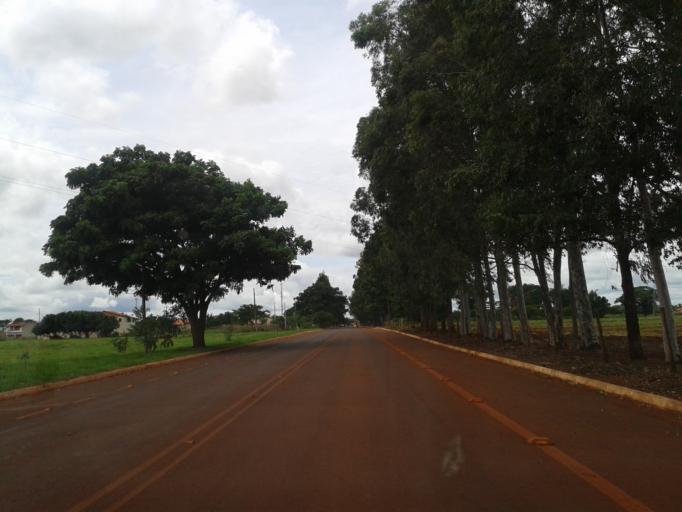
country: BR
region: Minas Gerais
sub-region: Centralina
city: Centralina
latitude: -18.5900
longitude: -49.2067
